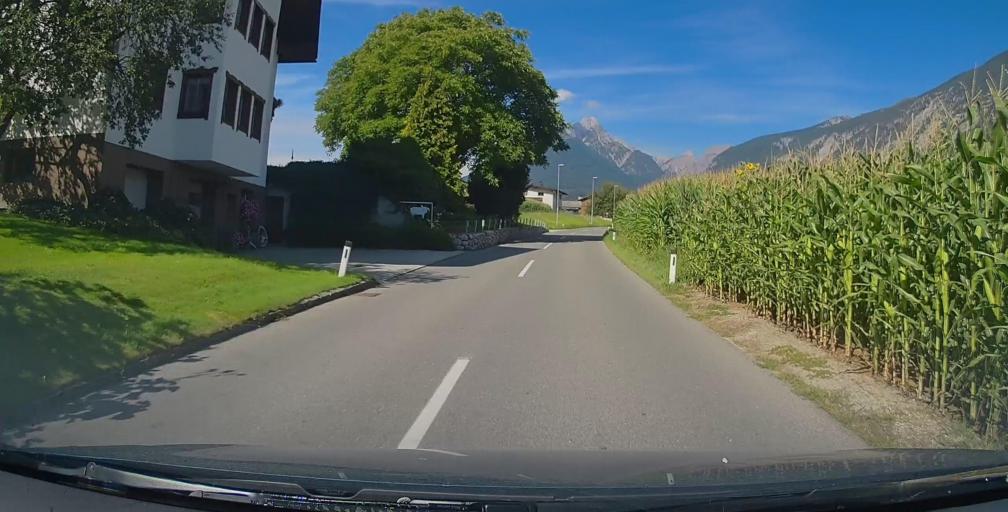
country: AT
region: Tyrol
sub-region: Politischer Bezirk Schwaz
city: Buch bei Jenbach
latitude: 47.3751
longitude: 11.7601
